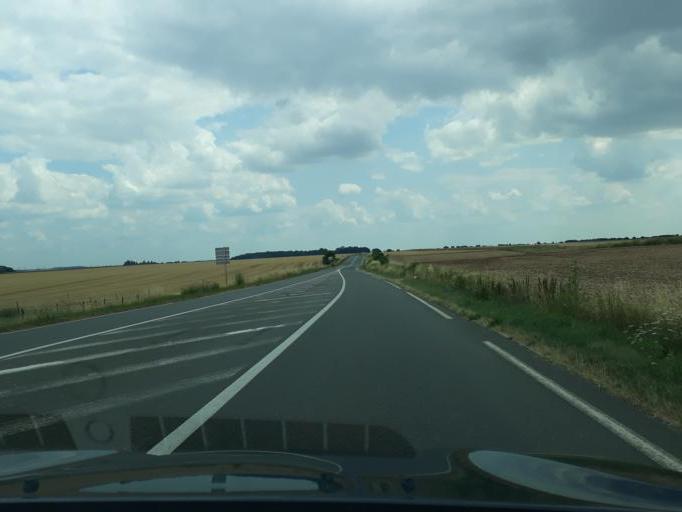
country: FR
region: Centre
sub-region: Departement du Cher
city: Avord
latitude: 47.0303
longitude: 2.6538
